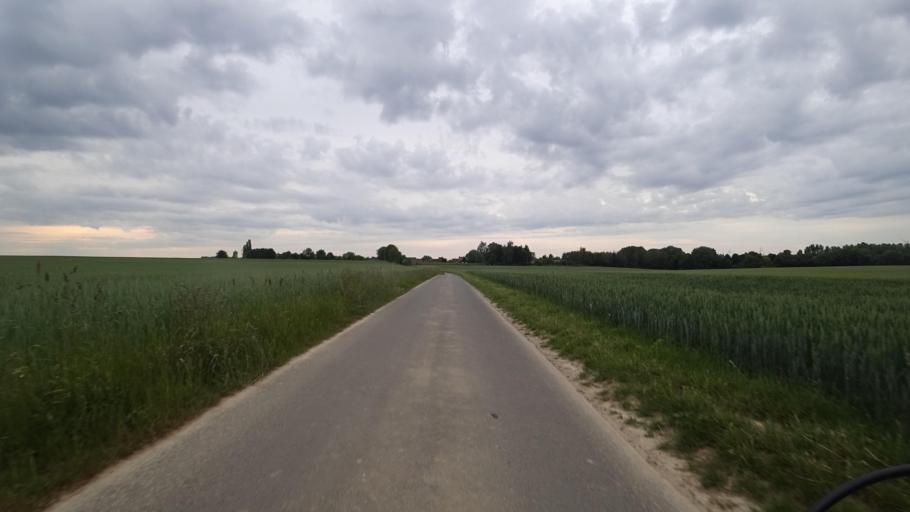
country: BE
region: Wallonia
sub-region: Province du Brabant Wallon
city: Perwez
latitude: 50.5666
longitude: 4.7723
